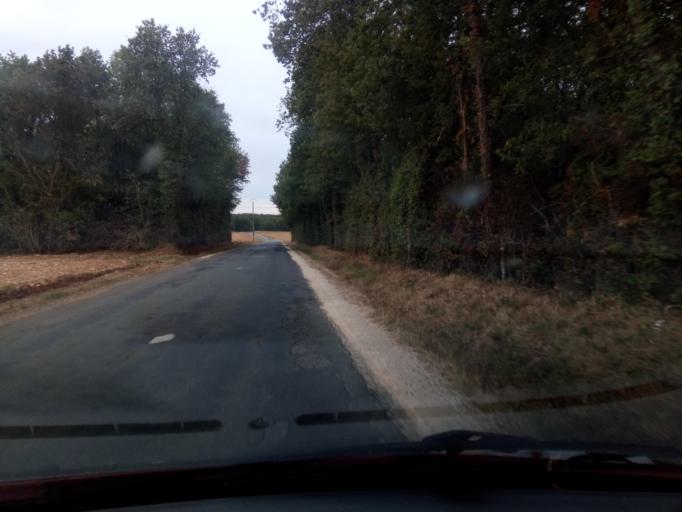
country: FR
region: Poitou-Charentes
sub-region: Departement de la Vienne
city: Saint-Savin
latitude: 46.5306
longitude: 0.7768
